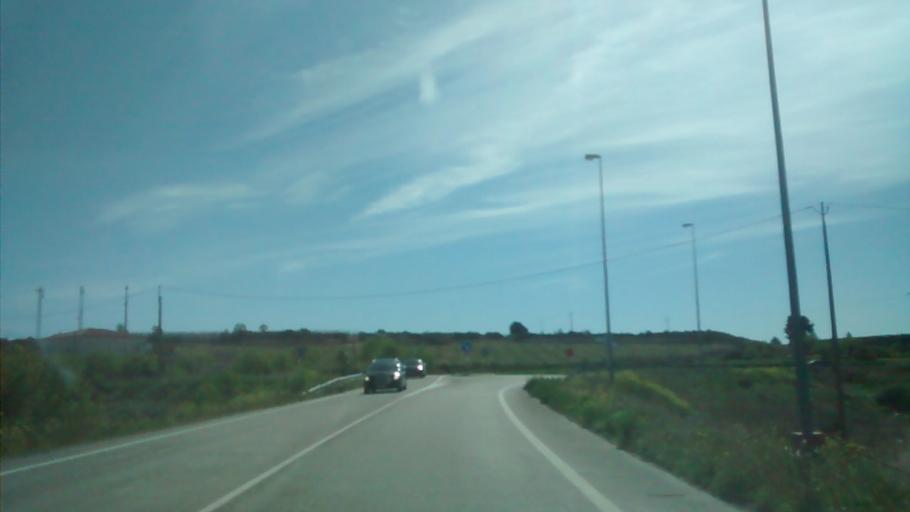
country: ES
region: Catalonia
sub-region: Provincia de Lleida
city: Maials
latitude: 41.3639
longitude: 0.5128
